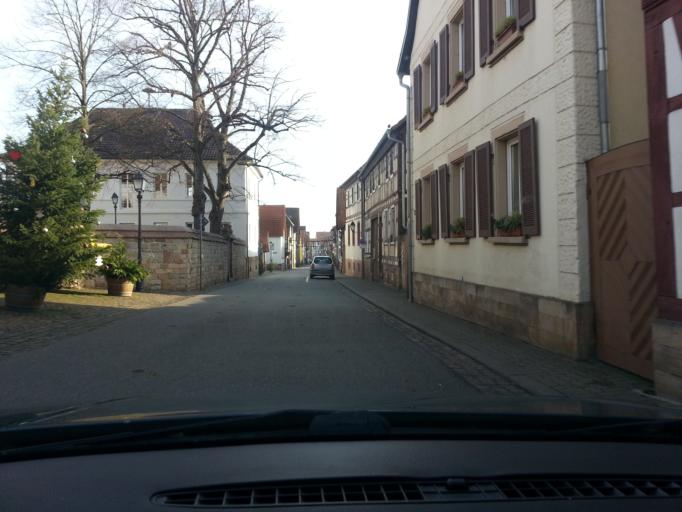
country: DE
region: Rheinland-Pfalz
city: Heuchelheim-Klingen
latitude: 49.1467
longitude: 8.0535
